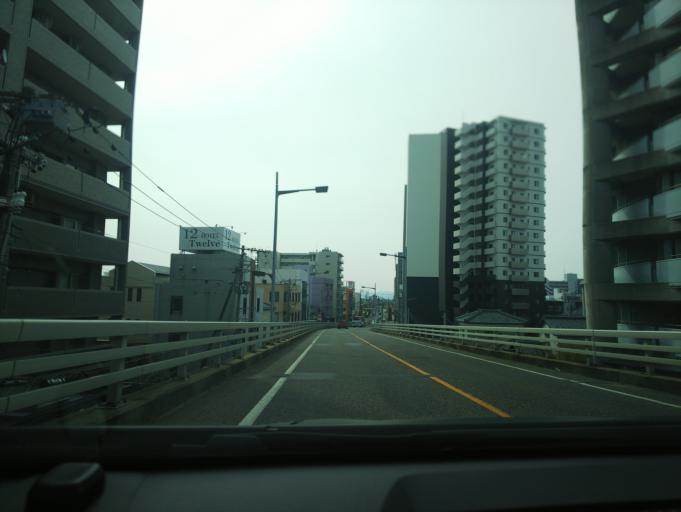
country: JP
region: Niigata
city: Niigata-shi
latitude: 37.9130
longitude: 139.0671
